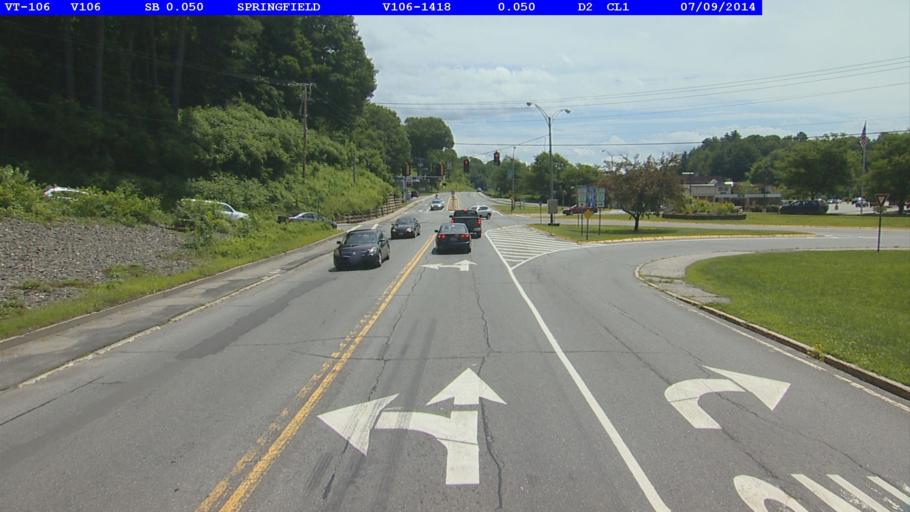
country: US
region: Vermont
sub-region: Windsor County
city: Springfield
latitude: 43.3044
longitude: -72.4922
